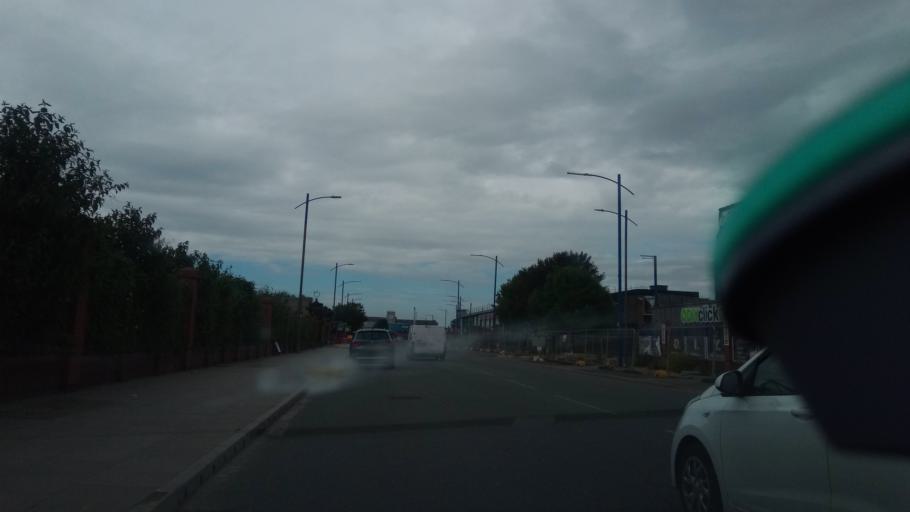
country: GB
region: England
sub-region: Liverpool
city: Liverpool
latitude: 53.4233
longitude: -2.9967
